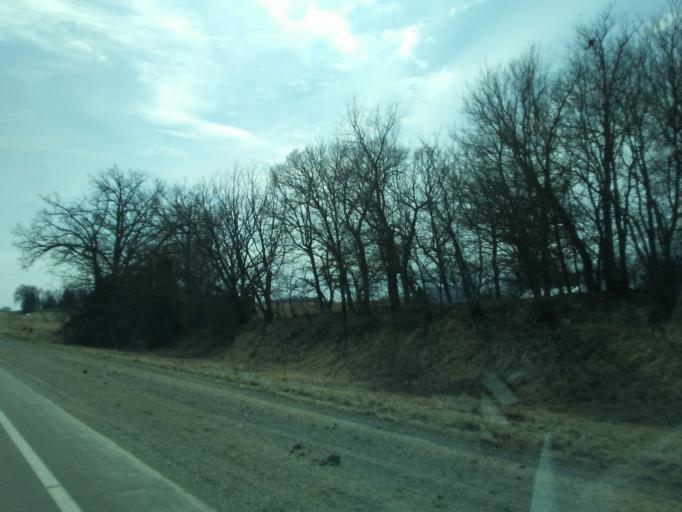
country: US
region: Iowa
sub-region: Winneshiek County
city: Decorah
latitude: 43.4276
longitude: -91.8594
